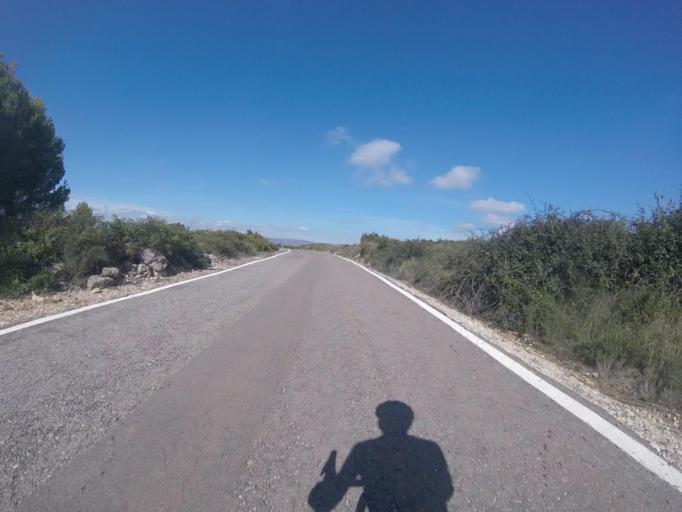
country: ES
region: Valencia
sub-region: Provincia de Castello
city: Albocasser
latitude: 40.3442
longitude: 0.0494
